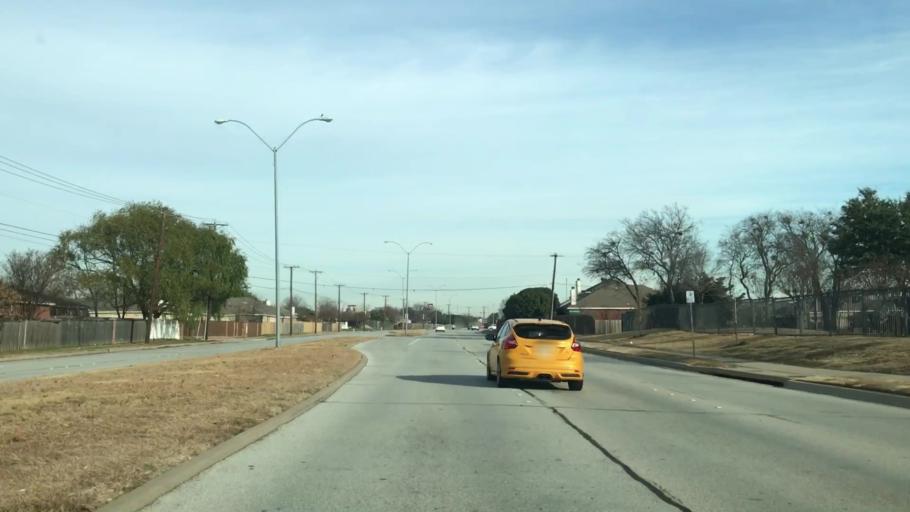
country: US
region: Texas
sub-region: Tarrant County
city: Watauga
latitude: 32.8678
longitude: -97.2912
